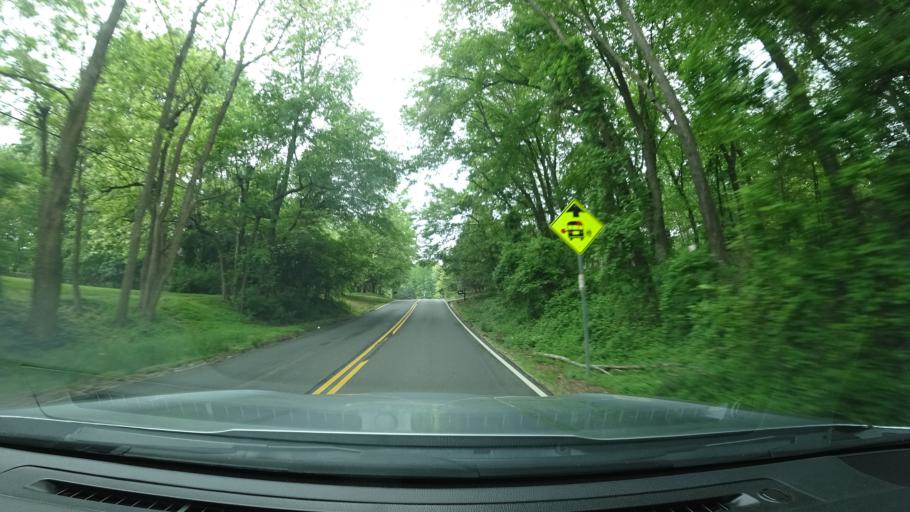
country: US
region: Virginia
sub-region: Fairfax County
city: Greenbriar
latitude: 38.8756
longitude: -77.3516
